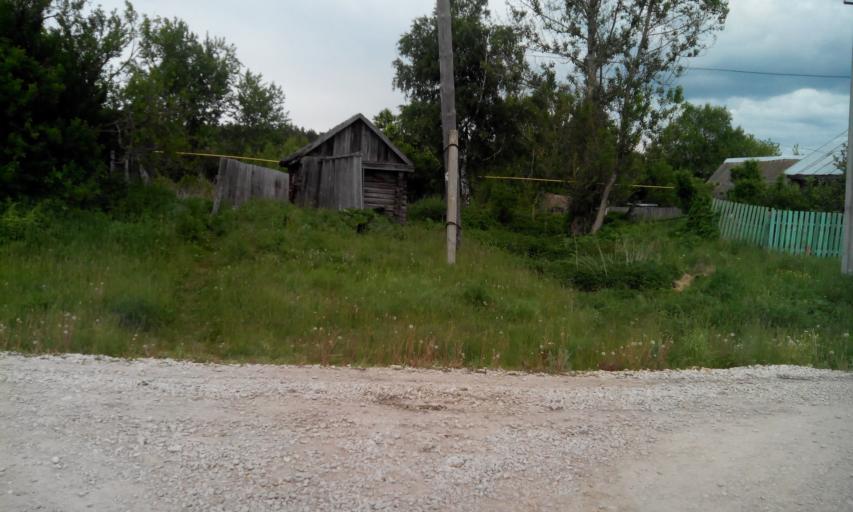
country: RU
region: Penza
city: Chaadayevka
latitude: 53.1832
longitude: 45.8638
